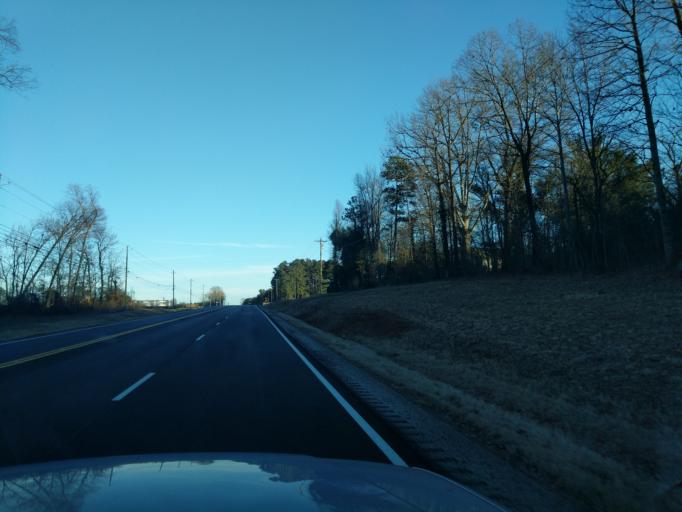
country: US
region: Georgia
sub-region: Stephens County
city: Toccoa
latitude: 34.5169
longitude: -83.2327
